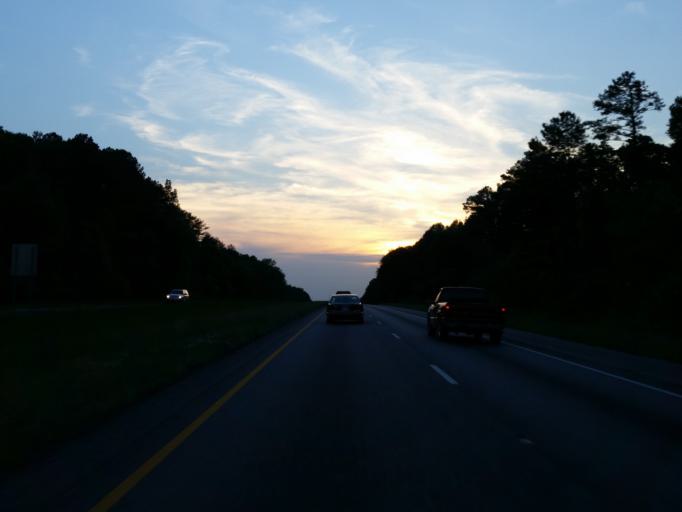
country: US
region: Alabama
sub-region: Calhoun County
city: Choccolocco
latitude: 33.6139
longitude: -85.6809
